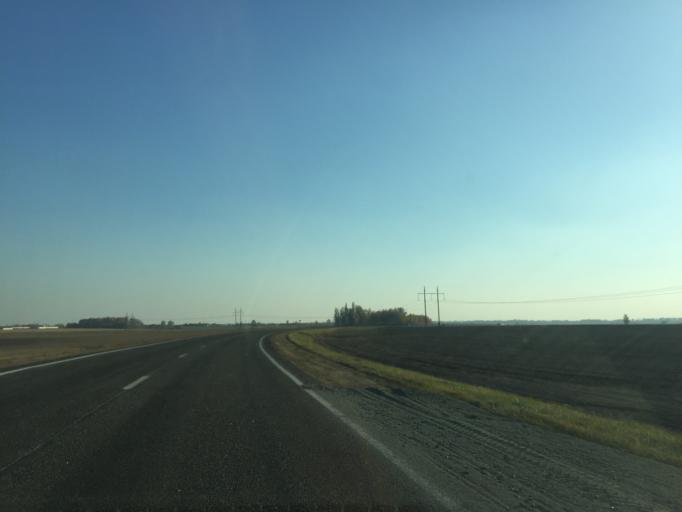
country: BY
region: Gomel
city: Dobrush
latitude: 52.3235
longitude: 31.2454
